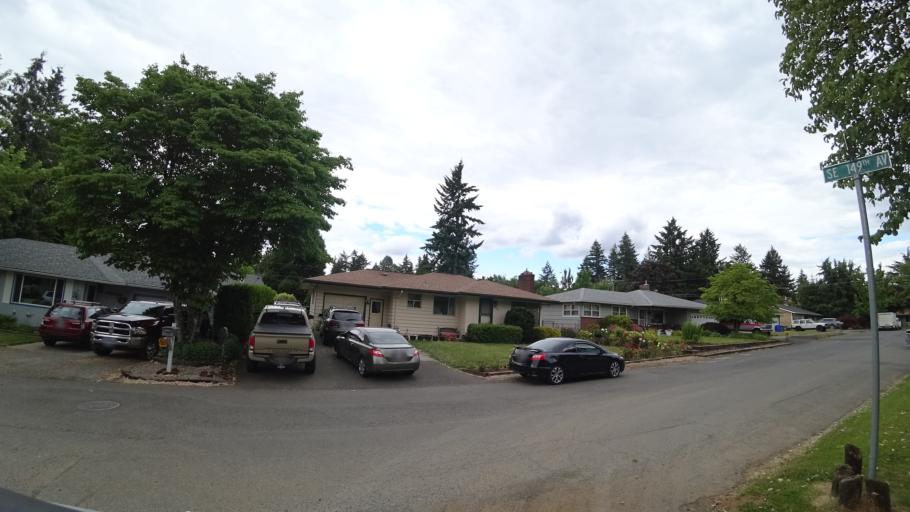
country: US
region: Oregon
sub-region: Clackamas County
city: Happy Valley
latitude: 45.4960
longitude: -122.5097
